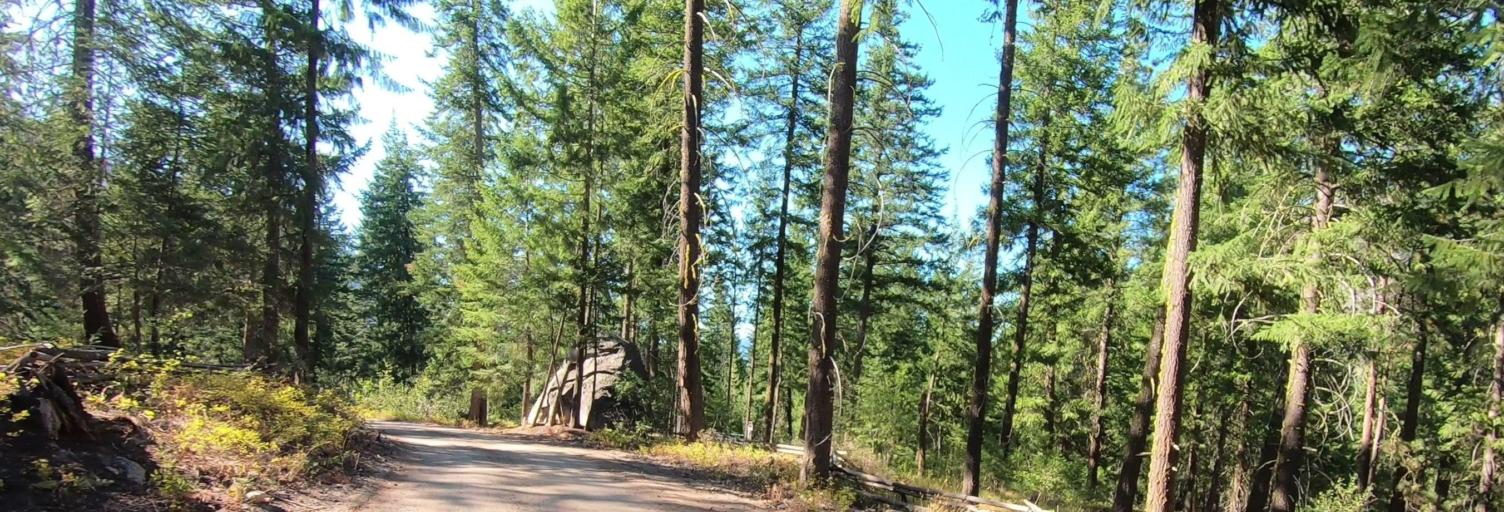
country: US
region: Washington
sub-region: Chelan County
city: Granite Falls
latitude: 48.5235
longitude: -120.3092
